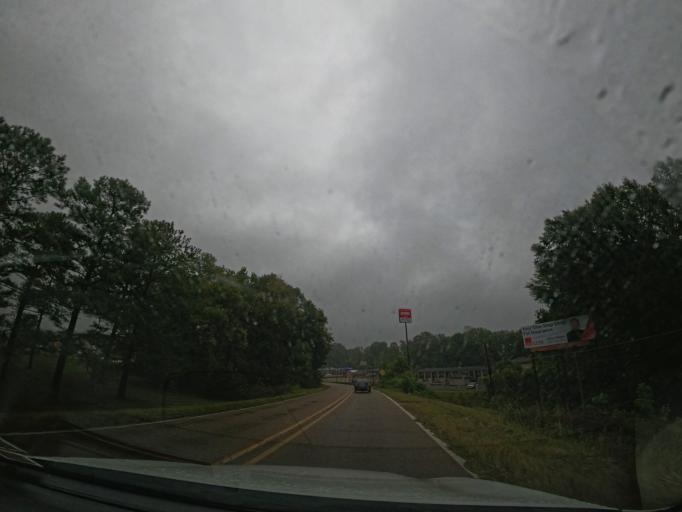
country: US
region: Mississippi
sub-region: Warren County
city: Vicksburg
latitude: 32.3252
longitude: -90.8634
